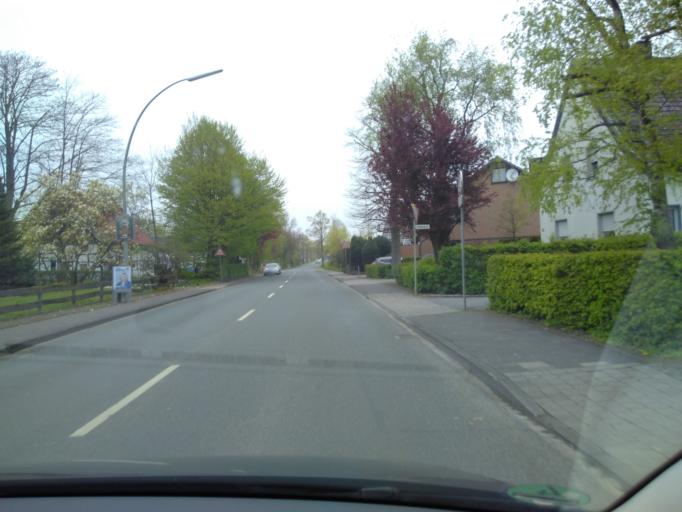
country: DE
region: North Rhine-Westphalia
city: Oelde
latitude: 51.7692
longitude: 8.1543
